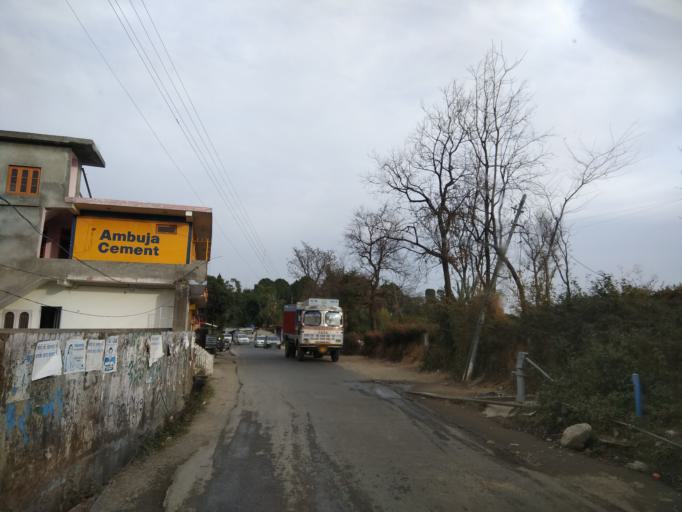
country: IN
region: Himachal Pradesh
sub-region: Kangra
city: Palampur
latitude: 32.1142
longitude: 76.5177
